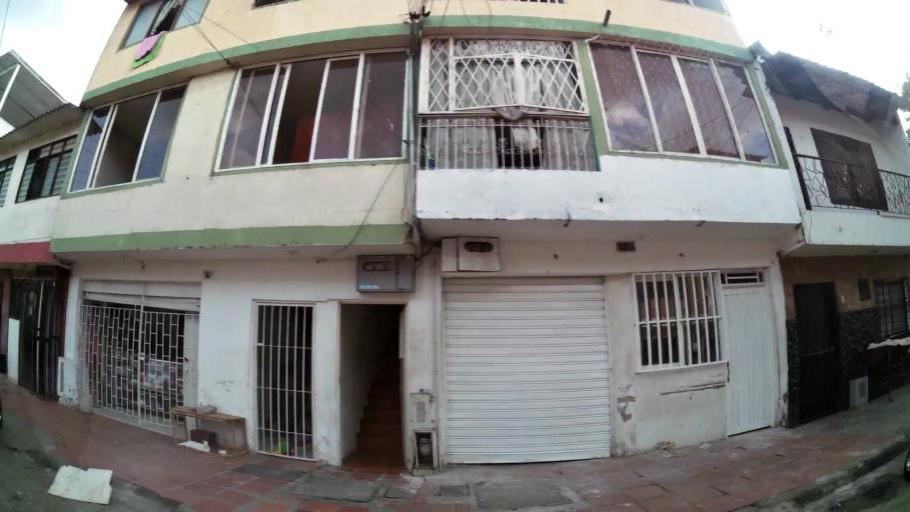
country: CO
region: Valle del Cauca
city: Cali
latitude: 3.4737
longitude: -76.5089
